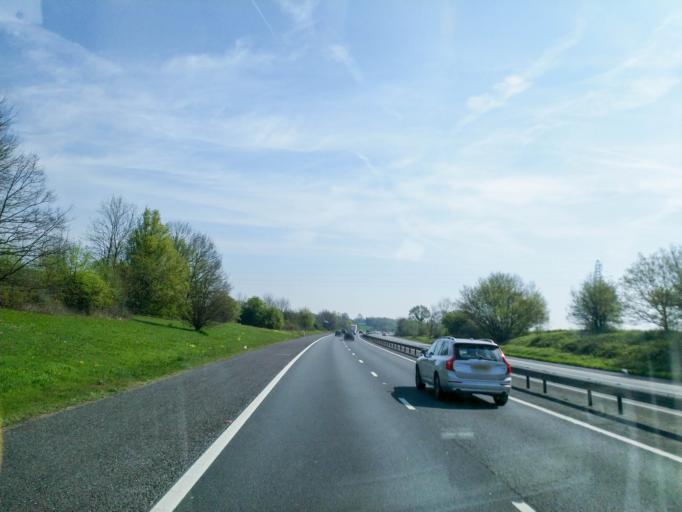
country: GB
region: England
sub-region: Kent
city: Borough Green
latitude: 51.3030
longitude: 0.2899
